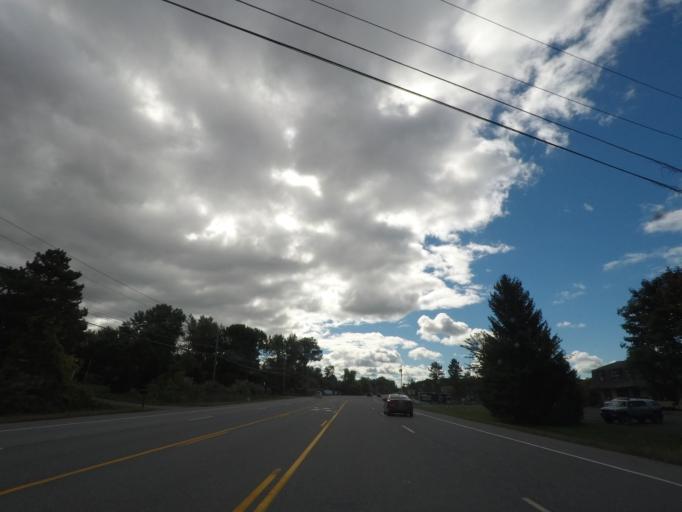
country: US
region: New York
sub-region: Albany County
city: Cohoes
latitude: 42.8024
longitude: -73.7336
